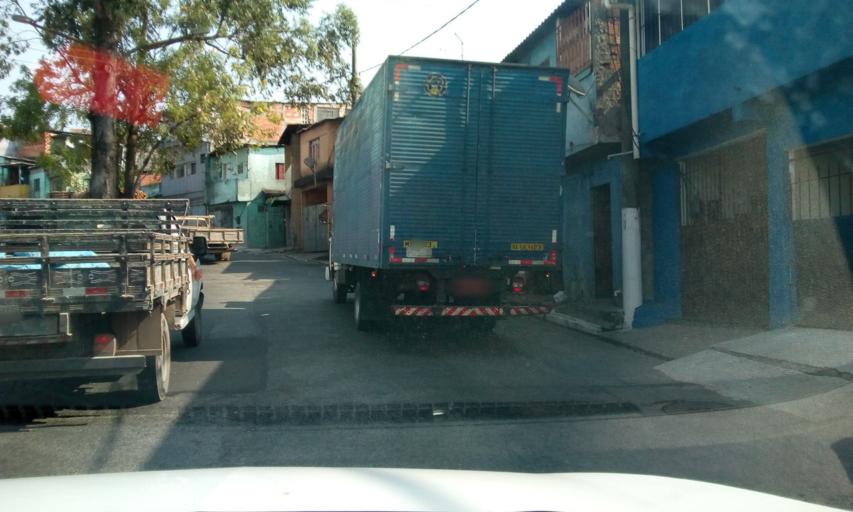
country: BR
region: Sao Paulo
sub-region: Diadema
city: Diadema
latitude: -23.7096
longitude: -46.6891
